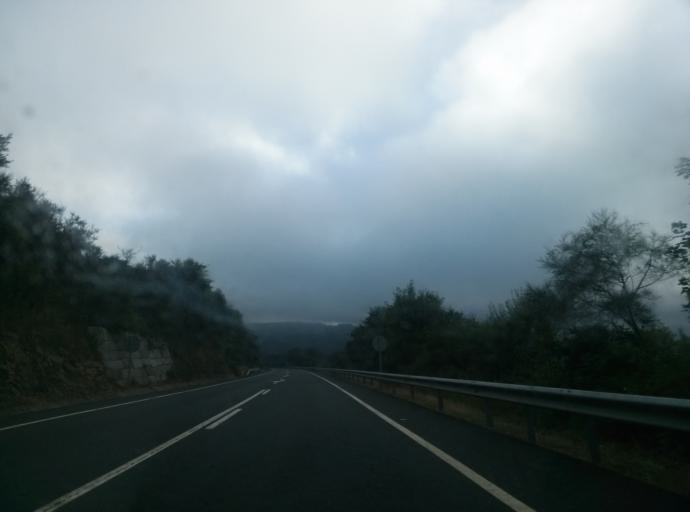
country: ES
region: Galicia
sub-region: Provincia de Lugo
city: Muras
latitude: 43.4647
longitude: -7.7068
